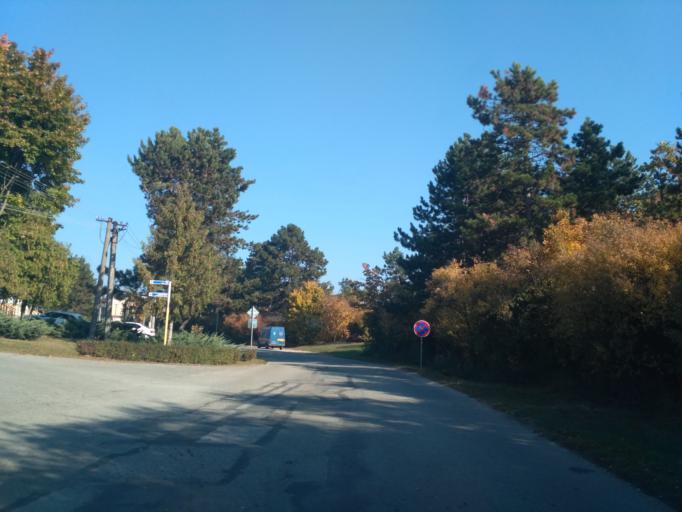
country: SK
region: Kosicky
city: Moldava nad Bodvou
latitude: 48.6115
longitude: 20.9909
